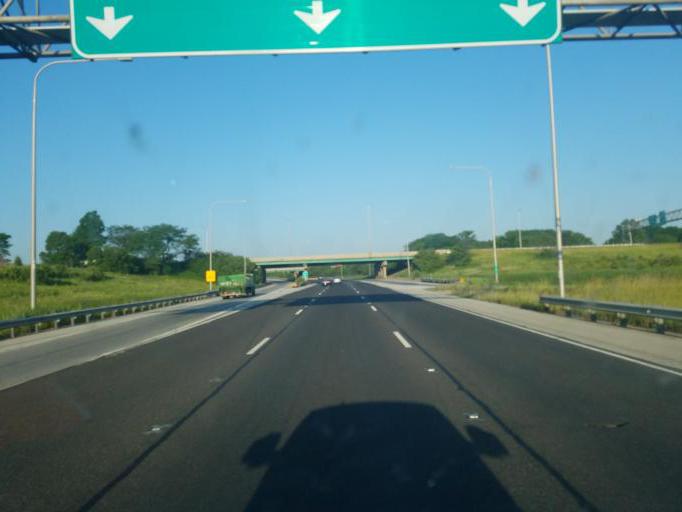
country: US
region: Illinois
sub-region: Cook County
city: Country Club Hills
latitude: 41.5677
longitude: -87.7408
